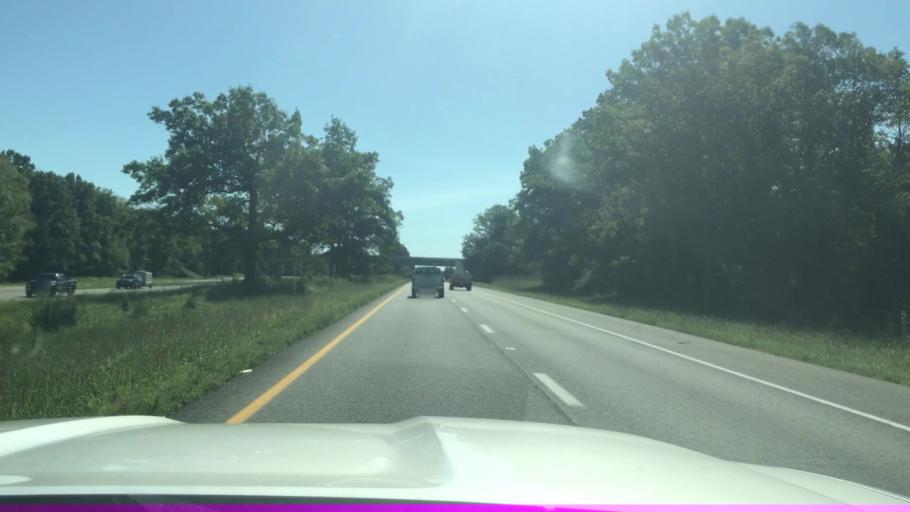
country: US
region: Virginia
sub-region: Henrico County
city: Sandston
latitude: 37.5243
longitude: -77.2839
